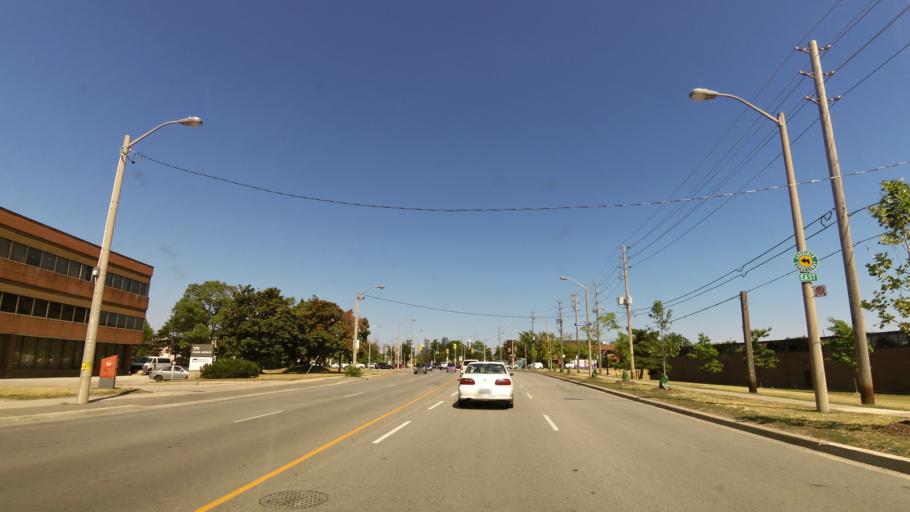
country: CA
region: Ontario
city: Etobicoke
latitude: 43.6181
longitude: -79.5130
